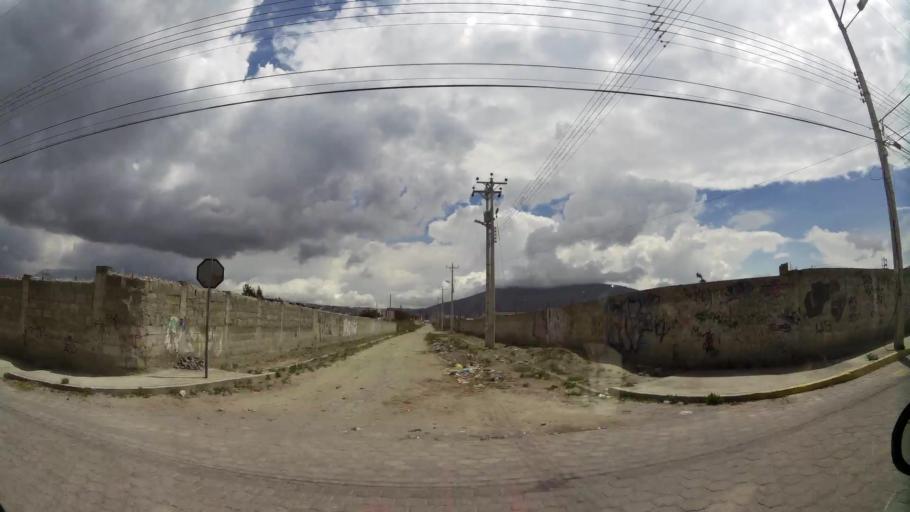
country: EC
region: Pichincha
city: Quito
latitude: -0.0651
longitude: -78.4145
